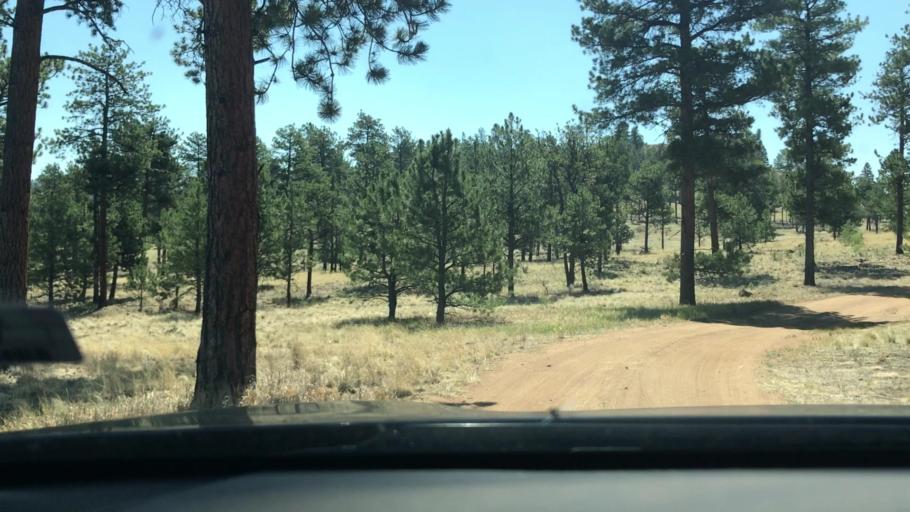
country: US
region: Colorado
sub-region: Teller County
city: Woodland Park
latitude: 38.9971
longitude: -105.3421
